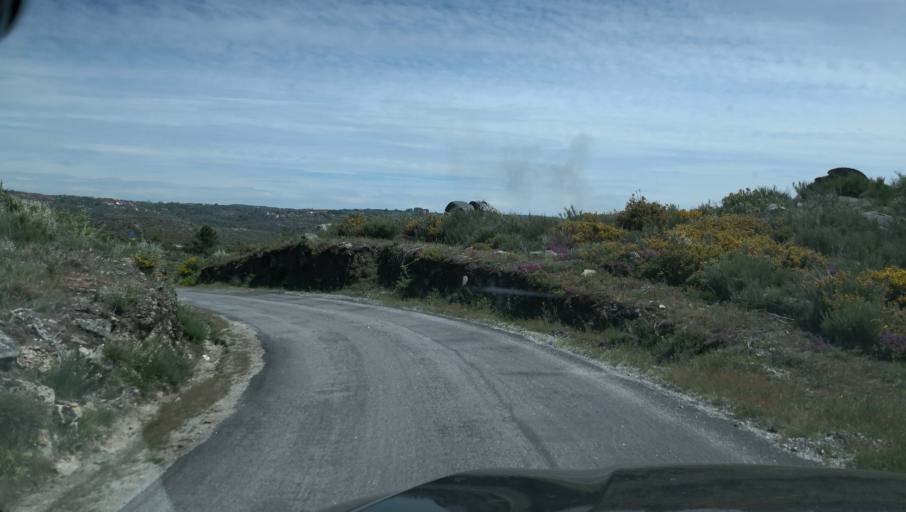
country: PT
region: Vila Real
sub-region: Vila Real
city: Vila Real
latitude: 41.3674
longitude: -7.6995
